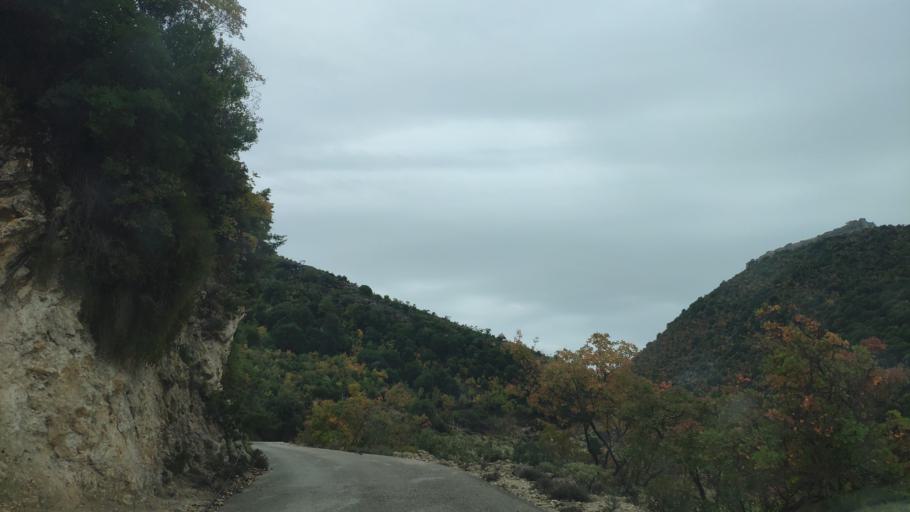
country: GR
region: Epirus
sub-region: Nomos Prevezis
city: Kanalaki
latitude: 39.3431
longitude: 20.6515
